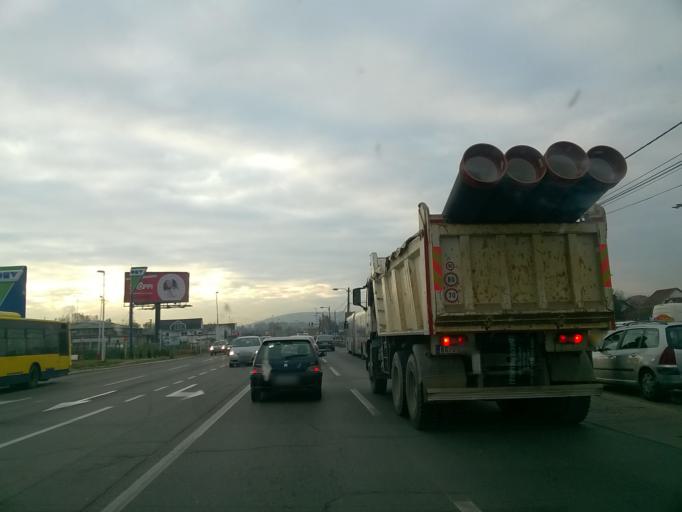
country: RS
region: Central Serbia
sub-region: Belgrade
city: Stari Grad
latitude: 44.8414
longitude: 20.4908
